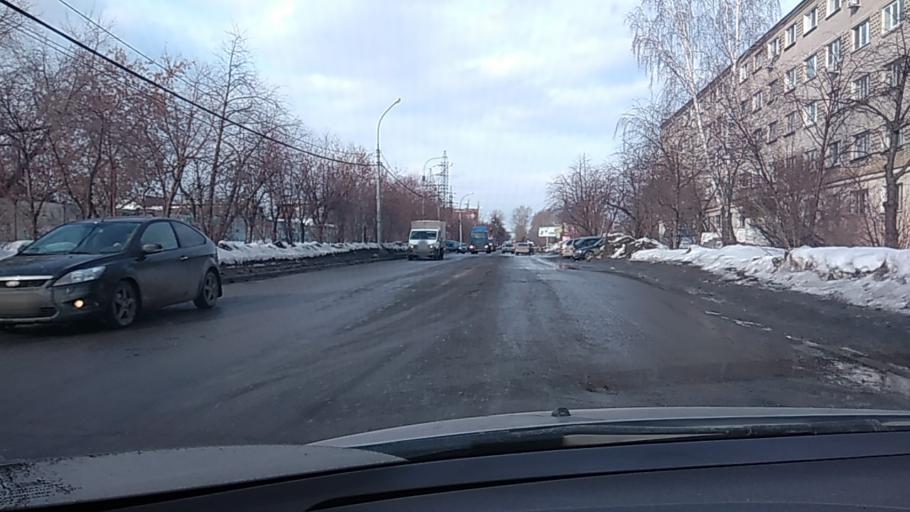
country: RU
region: Sverdlovsk
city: Yekaterinburg
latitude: 56.8653
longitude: 60.6529
